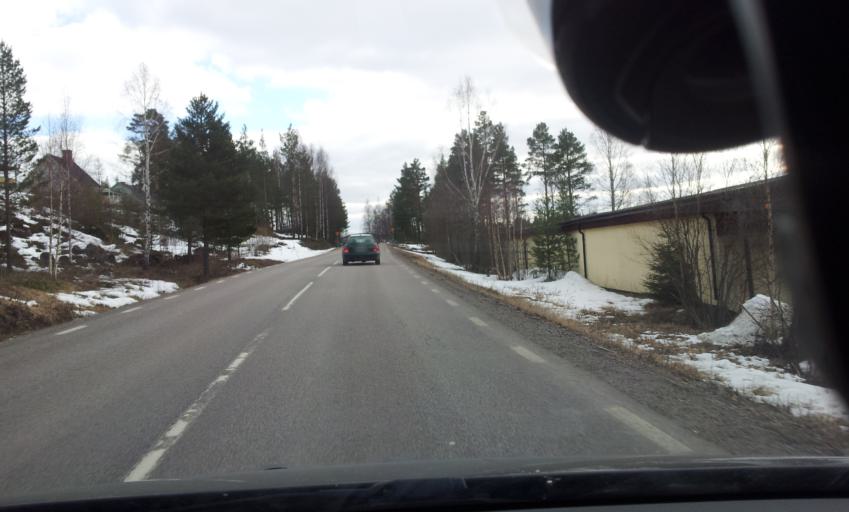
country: SE
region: Vaesternorrland
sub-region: Ange Kommun
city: Ange
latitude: 62.1590
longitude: 15.6771
